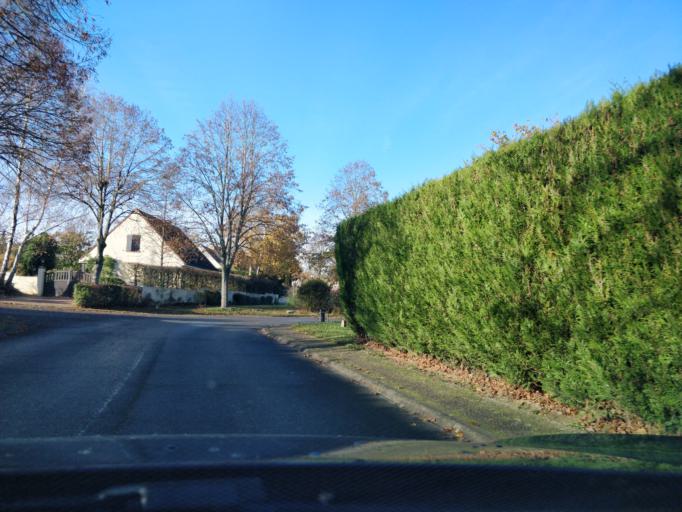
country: FR
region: Ile-de-France
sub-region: Departement de l'Essonne
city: Limours
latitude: 48.6386
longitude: 2.0805
